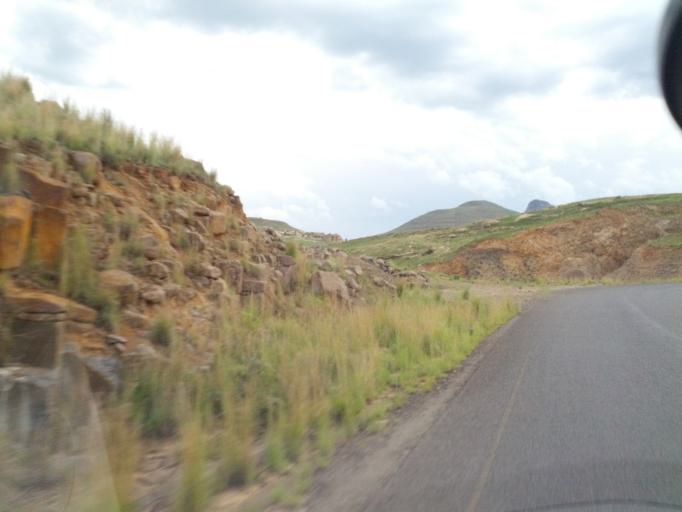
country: LS
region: Qacha's Nek
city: Qacha's Nek
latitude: -30.0698
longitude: 28.6013
